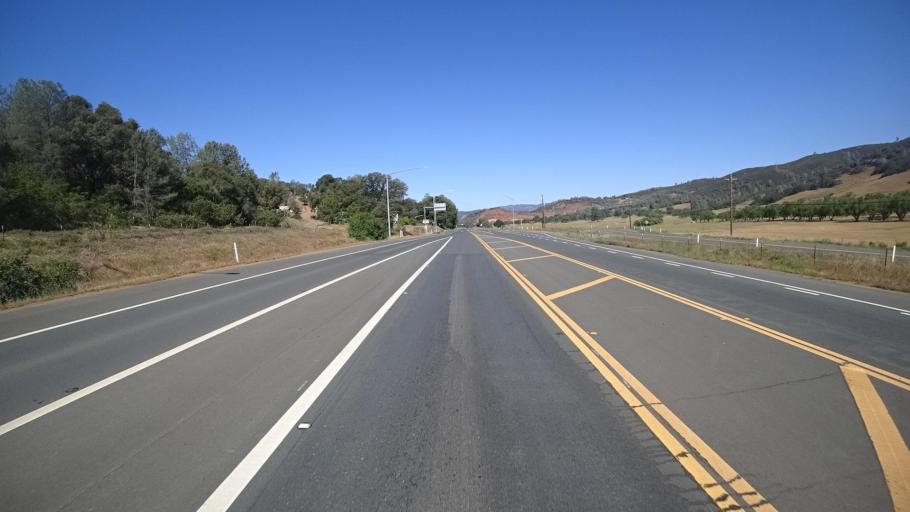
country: US
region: California
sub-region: Lake County
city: Clearlake
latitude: 39.0089
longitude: -122.6179
